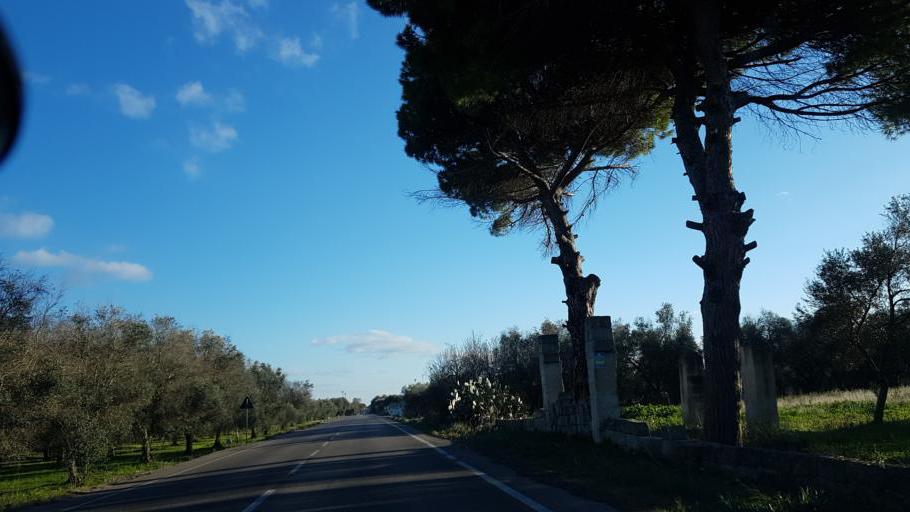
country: IT
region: Apulia
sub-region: Provincia di Lecce
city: Squinzano
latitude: 40.4520
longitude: 18.0274
